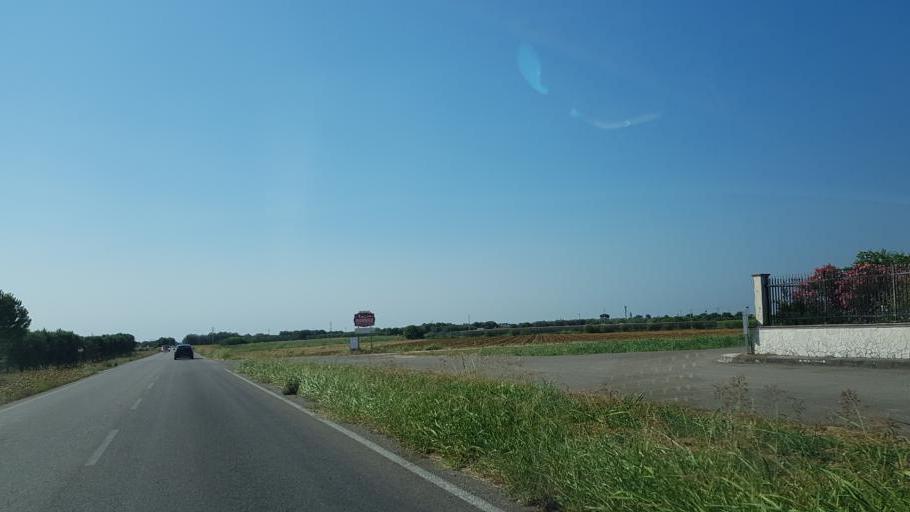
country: IT
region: Apulia
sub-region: Provincia di Lecce
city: Guagnano
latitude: 40.4092
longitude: 17.9626
